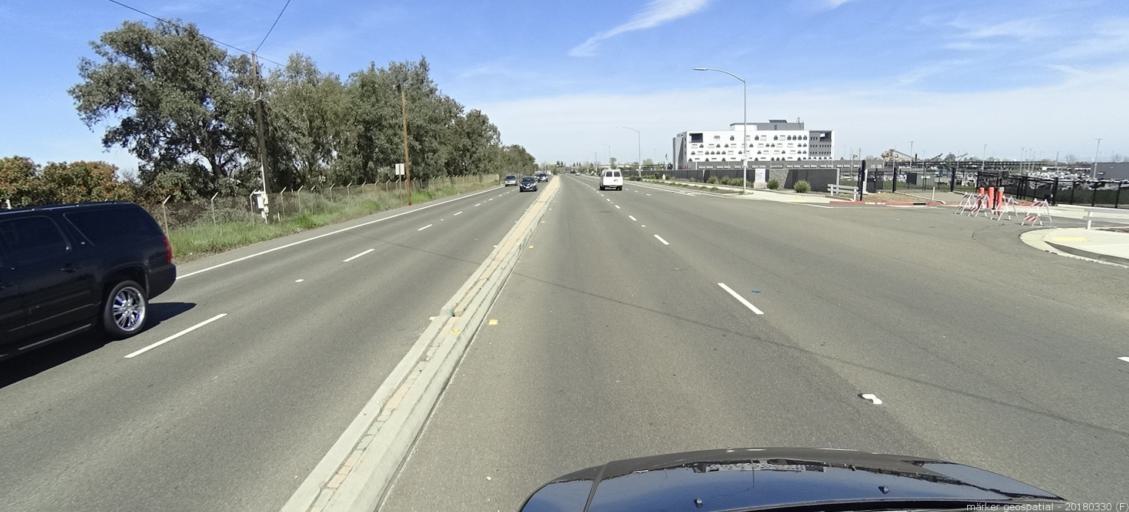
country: US
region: California
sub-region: Sacramento County
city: Rosemont
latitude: 38.5398
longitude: -121.3349
